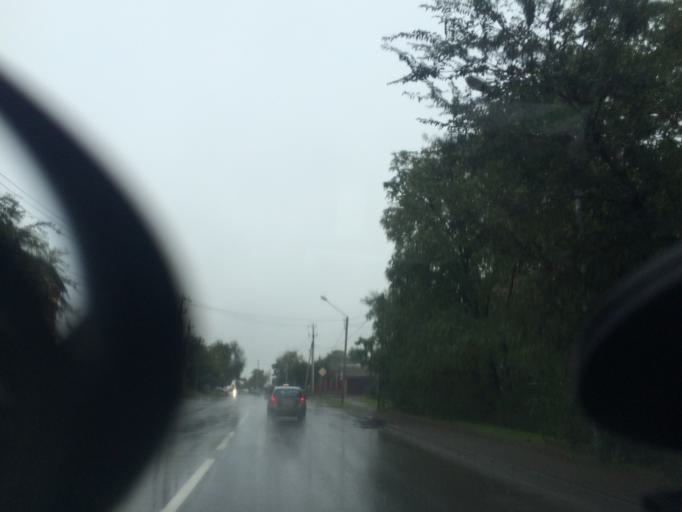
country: RU
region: Rostov
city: Rostov-na-Donu
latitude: 47.1938
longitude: 39.6158
